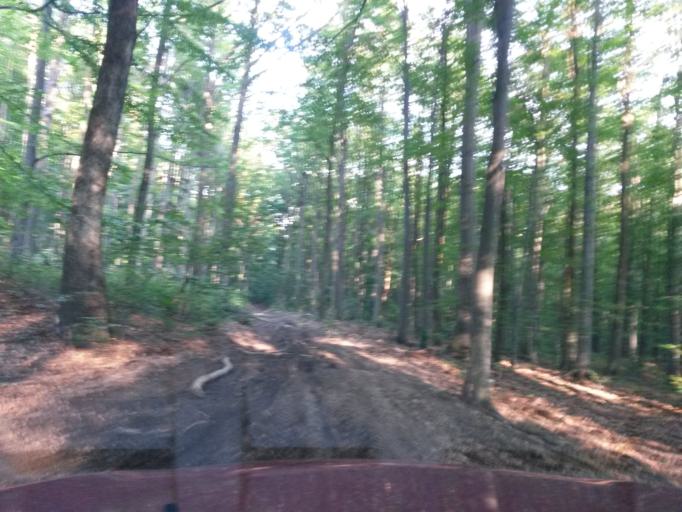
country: SK
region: Kosicky
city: Moldava nad Bodvou
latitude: 48.7306
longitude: 21.0483
